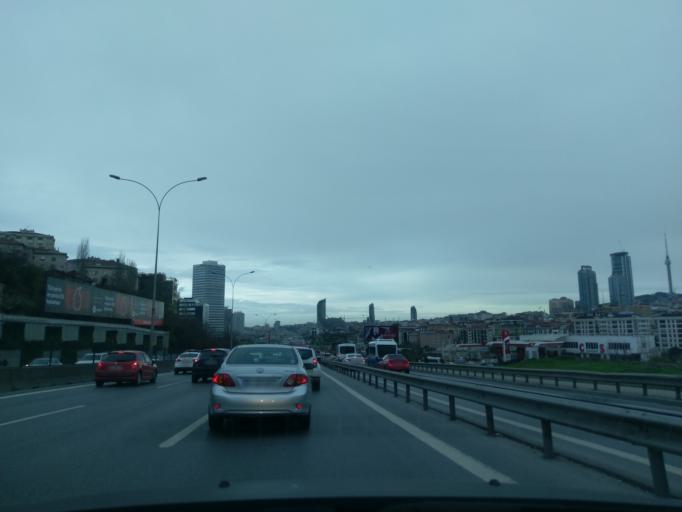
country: TR
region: Istanbul
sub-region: Atasehir
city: Atasehir
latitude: 40.9889
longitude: 29.0833
